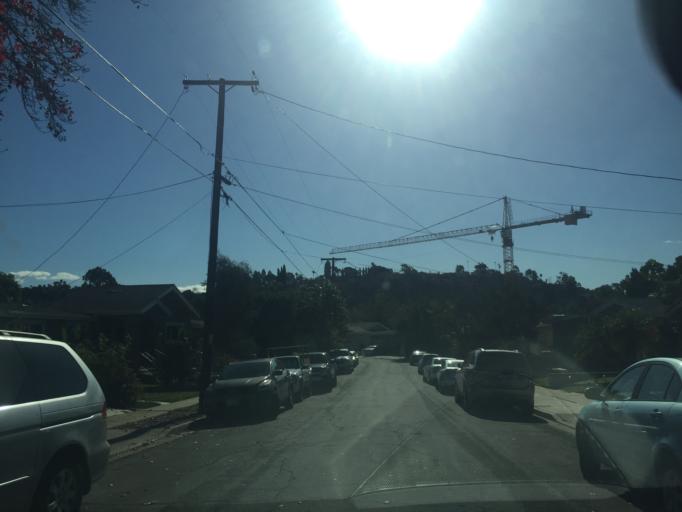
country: US
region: California
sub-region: San Diego County
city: La Mesa
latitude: 32.7848
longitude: -117.0955
